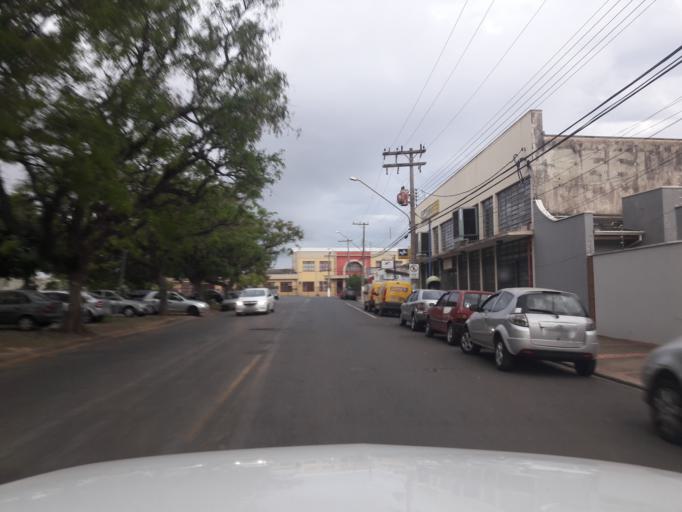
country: BR
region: Sao Paulo
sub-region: Moji-Guacu
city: Mogi-Gaucu
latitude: -22.3665
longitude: -46.9490
